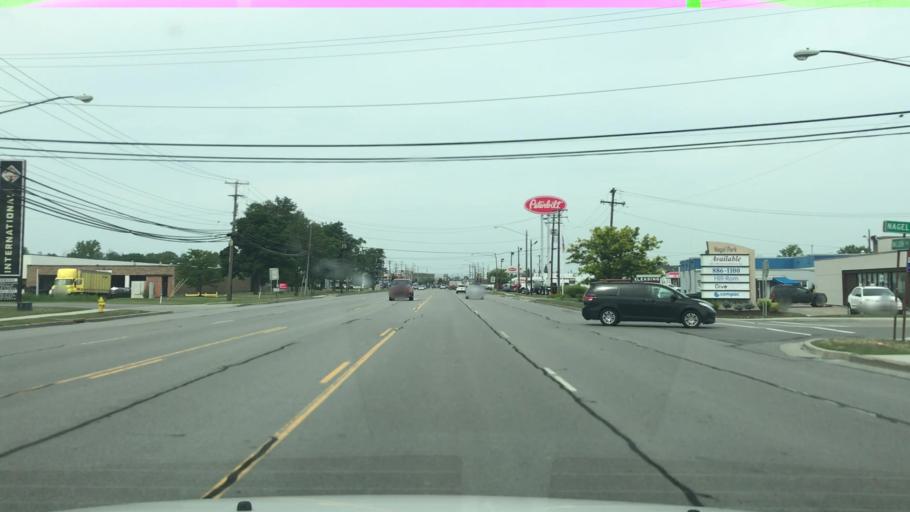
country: US
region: New York
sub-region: Erie County
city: Cheektowaga
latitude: 42.9079
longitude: -78.7466
